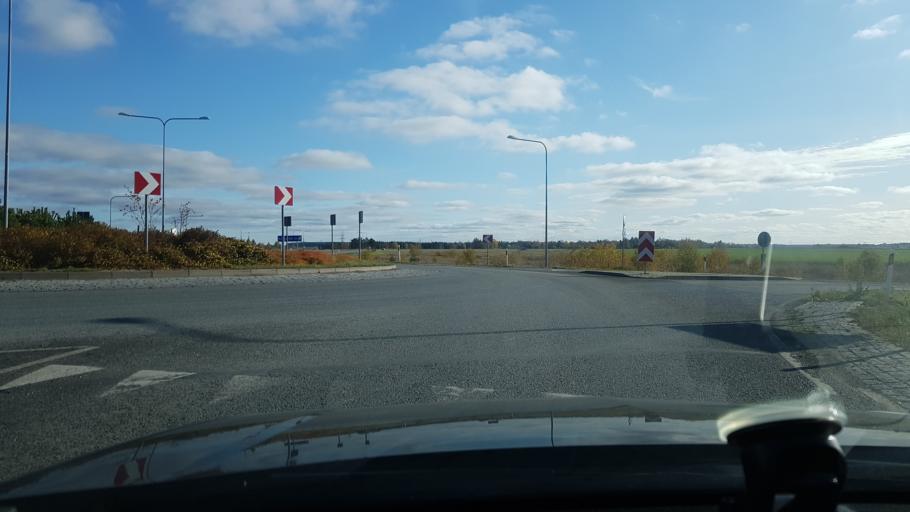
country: EE
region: Laeaene-Virumaa
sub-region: Haljala vald
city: Haljala
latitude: 59.4225
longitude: 26.2690
